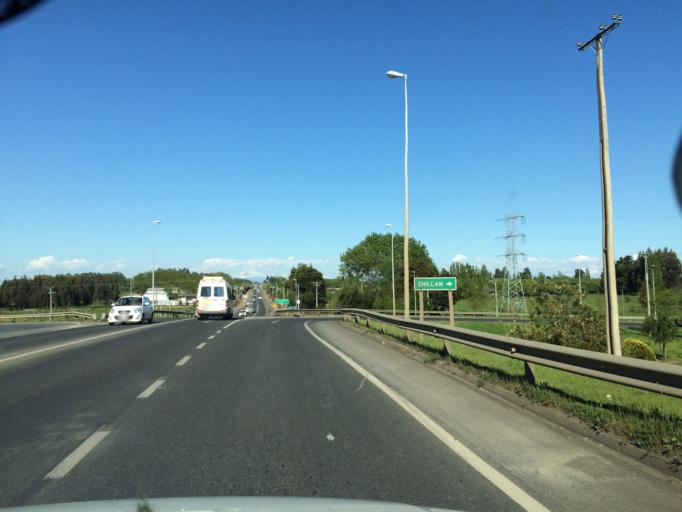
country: CL
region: Biobio
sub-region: Provincia de Biobio
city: Los Angeles
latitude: -37.4840
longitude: -72.4044
